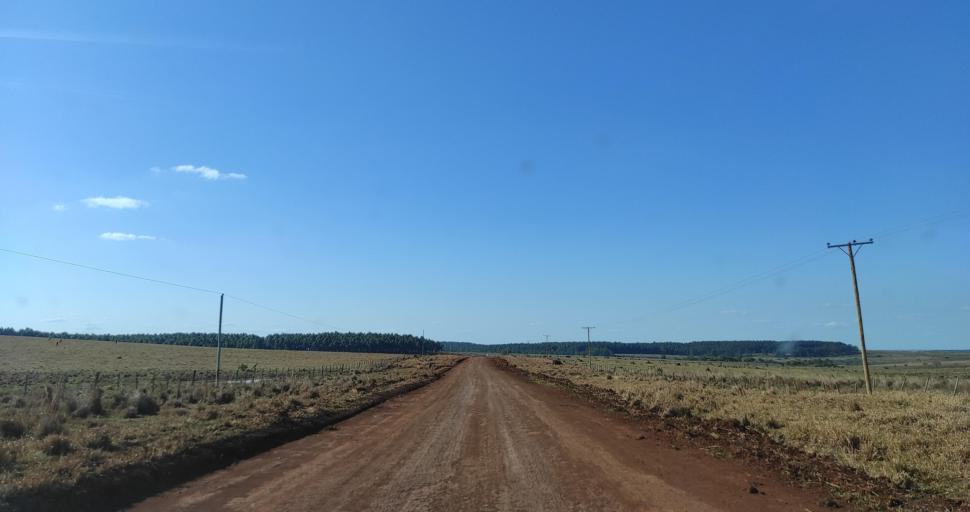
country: PY
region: Itapua
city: San Juan del Parana
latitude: -27.4303
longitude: -56.0837
